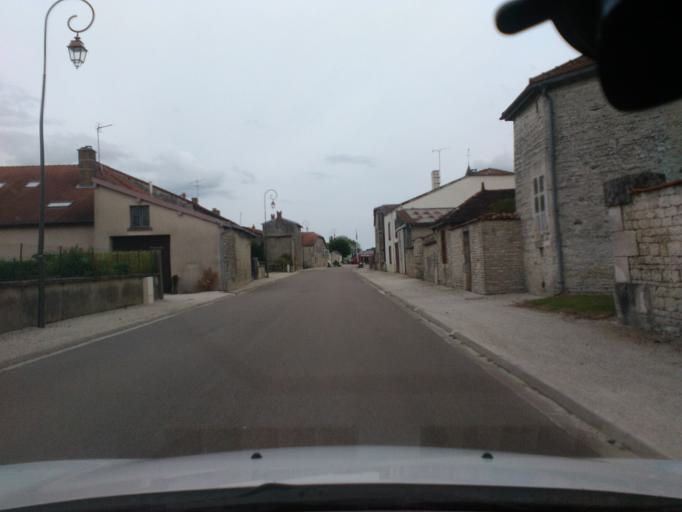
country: FR
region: Champagne-Ardenne
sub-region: Departement de l'Aube
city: Bar-sur-Aube
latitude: 48.2241
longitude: 4.8062
